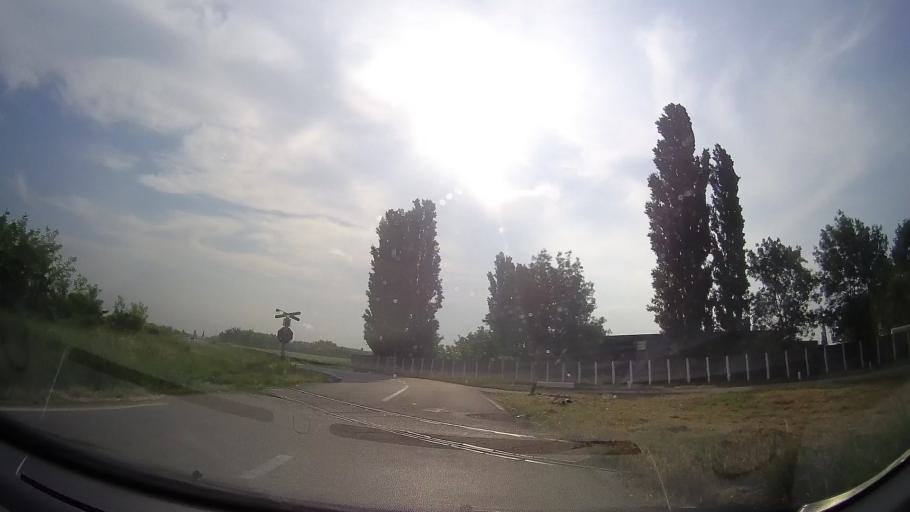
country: RO
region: Timis
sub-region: Comuna Parta
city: Parta
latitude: 45.6332
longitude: 21.1037
